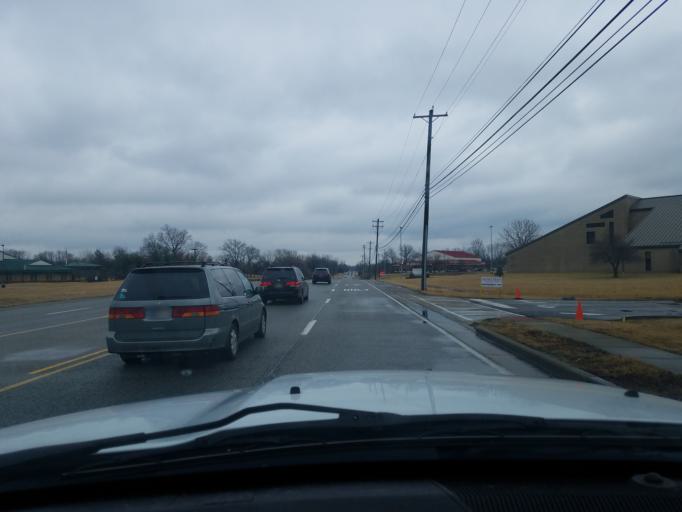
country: US
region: Indiana
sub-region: Clark County
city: Clarksville
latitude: 38.3292
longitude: -85.7350
